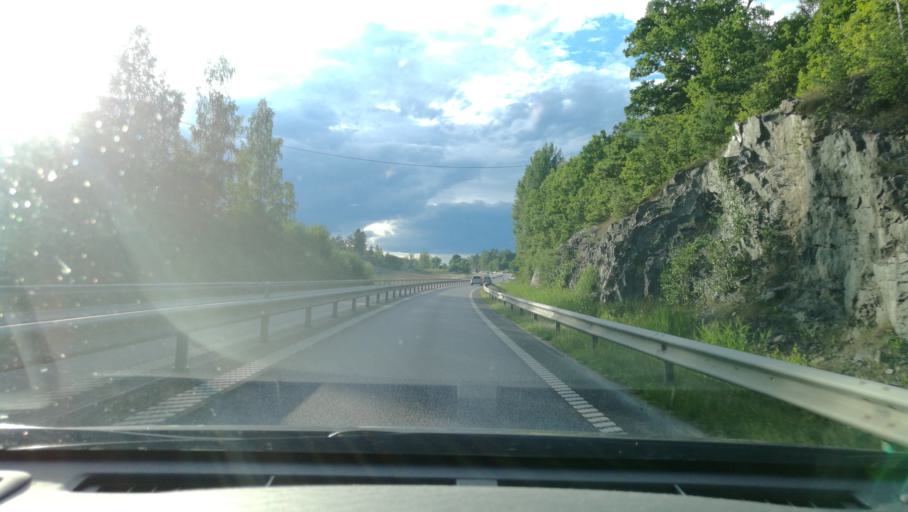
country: SE
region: OEstergoetland
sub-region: Norrkopings Kommun
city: Svartinge
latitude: 58.6818
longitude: 15.9405
